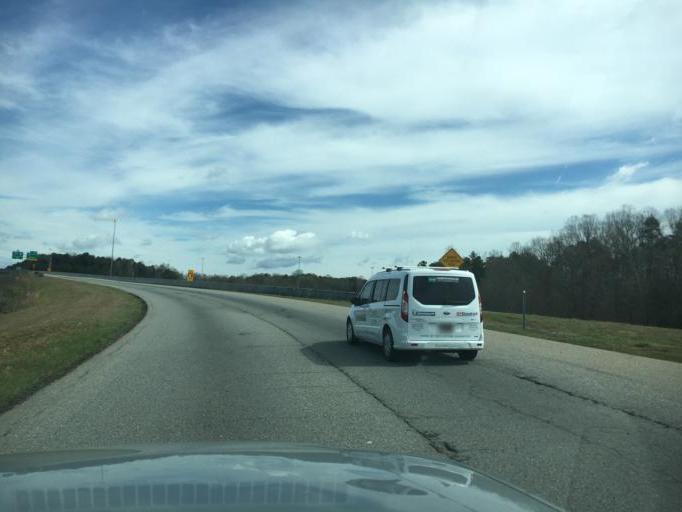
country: US
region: South Carolina
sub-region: Greenville County
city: Gantt
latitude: 34.7879
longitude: -82.4398
